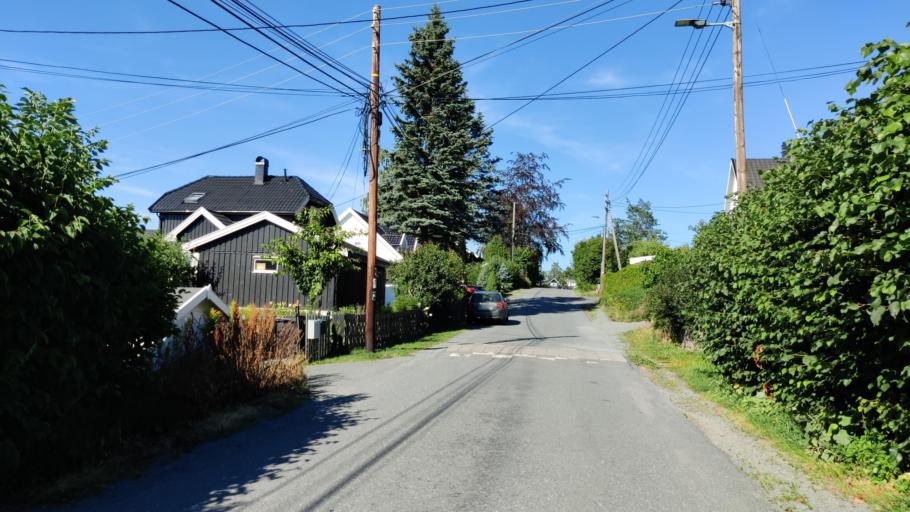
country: NO
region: Akershus
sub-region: Baerum
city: Lysaker
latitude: 59.9229
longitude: 10.5949
